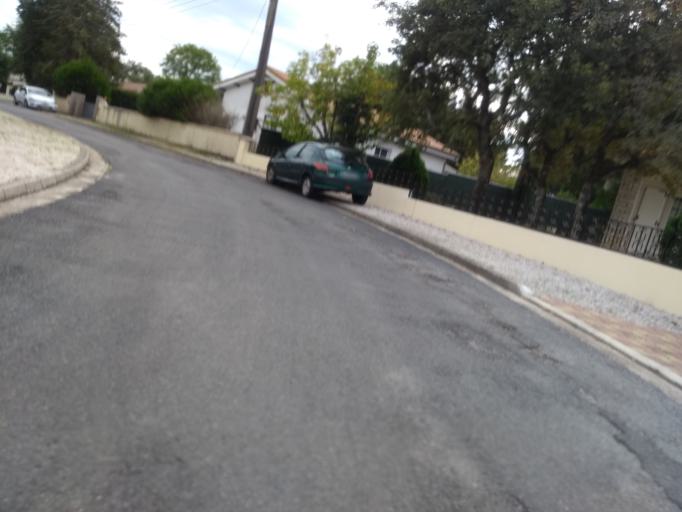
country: FR
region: Aquitaine
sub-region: Departement de la Gironde
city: Cestas
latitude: 44.7431
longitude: -0.6912
